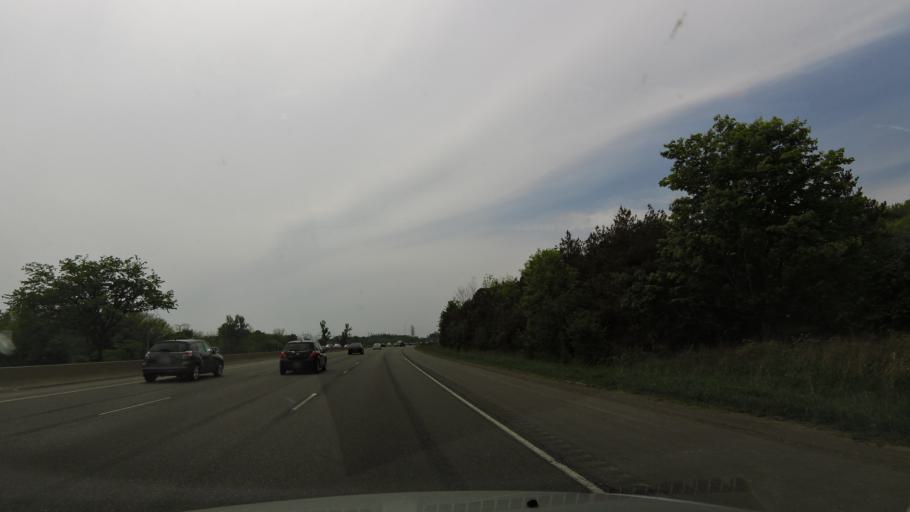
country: CA
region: Ontario
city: Oshawa
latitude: 43.8869
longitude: -78.7059
